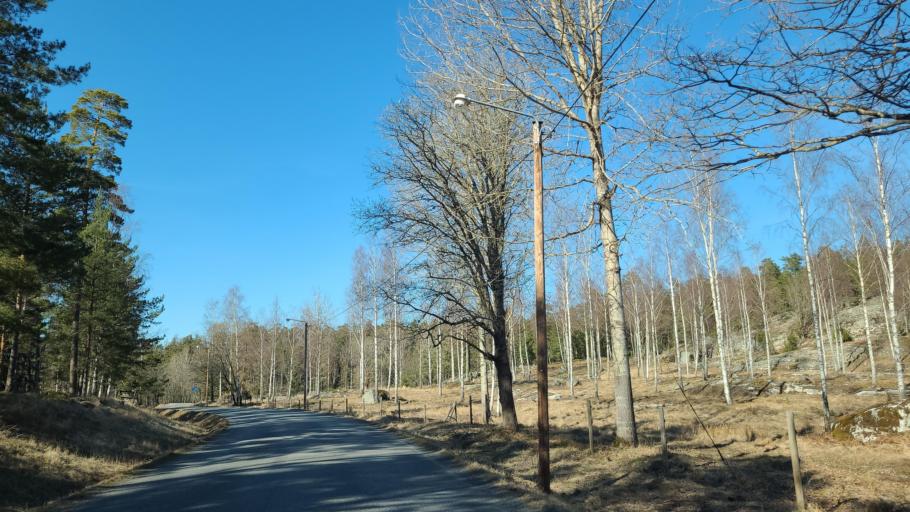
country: SE
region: Stockholm
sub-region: Varmdo Kommun
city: Hemmesta
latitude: 59.2798
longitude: 18.5700
